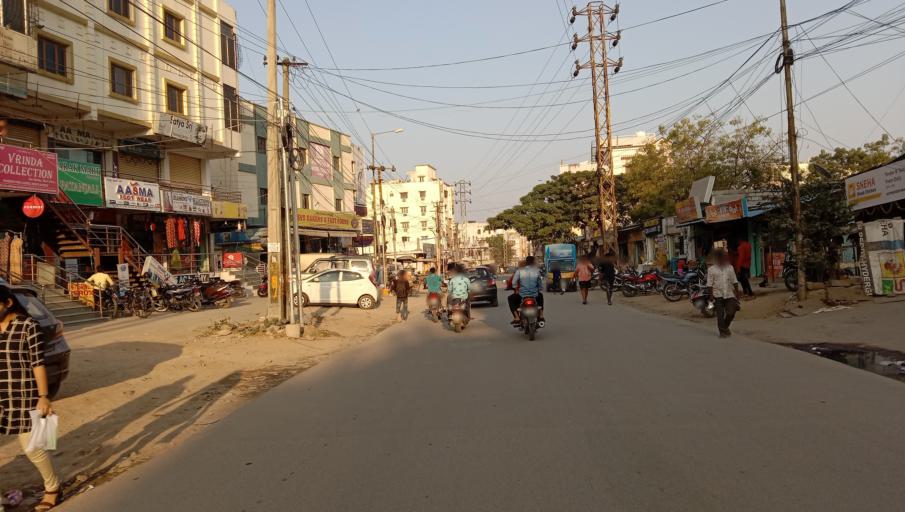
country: IN
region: Telangana
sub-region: Hyderabad
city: Hyderabad
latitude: 17.3634
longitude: 78.4235
